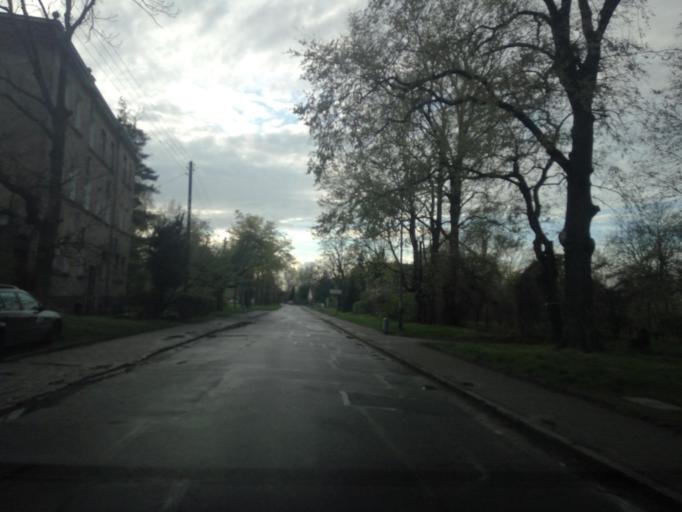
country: PL
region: Lower Silesian Voivodeship
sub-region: Powiat wroclawski
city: Radwanice
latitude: 51.0623
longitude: 17.0768
